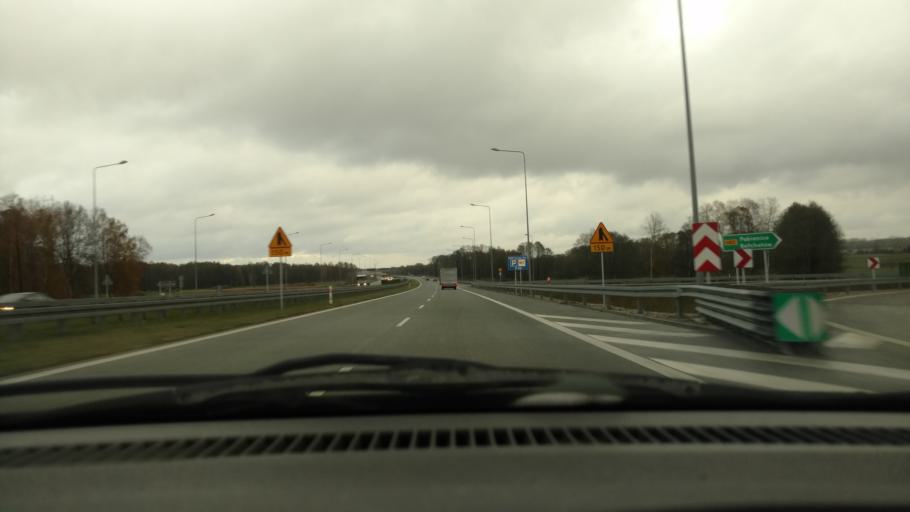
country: PL
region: Lodz Voivodeship
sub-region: Powiat pabianicki
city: Pabianice
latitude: 51.6139
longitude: 19.3668
